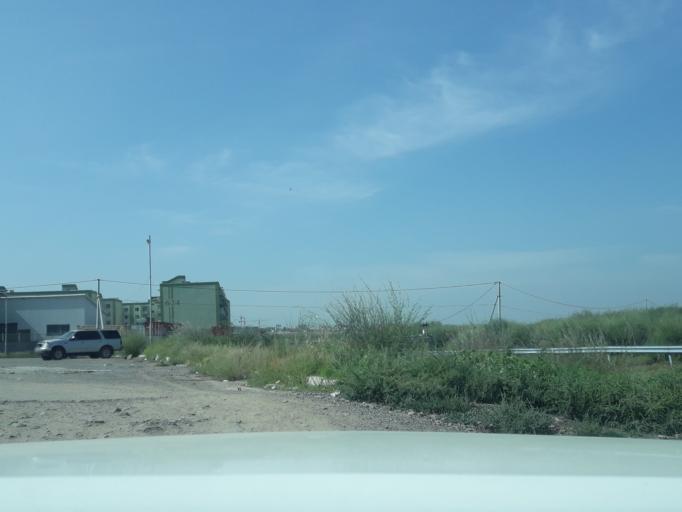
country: MN
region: Ulaanbaatar
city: Ulaanbaatar
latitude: 47.8808
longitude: 106.8486
